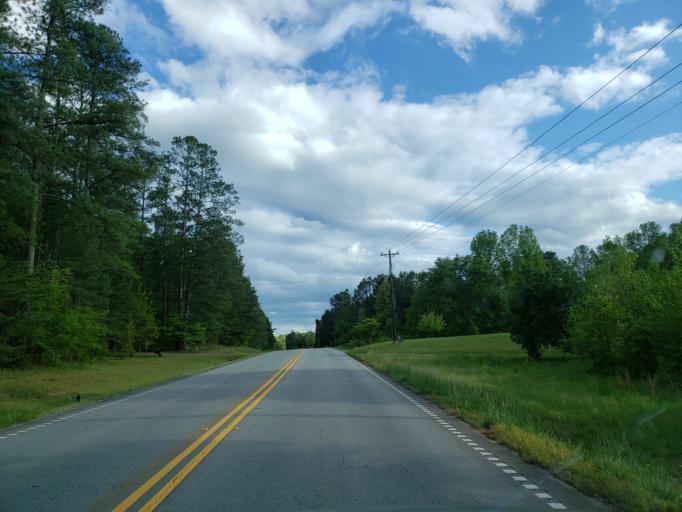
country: US
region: Georgia
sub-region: Haralson County
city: Tallapoosa
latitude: 33.8302
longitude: -85.2929
